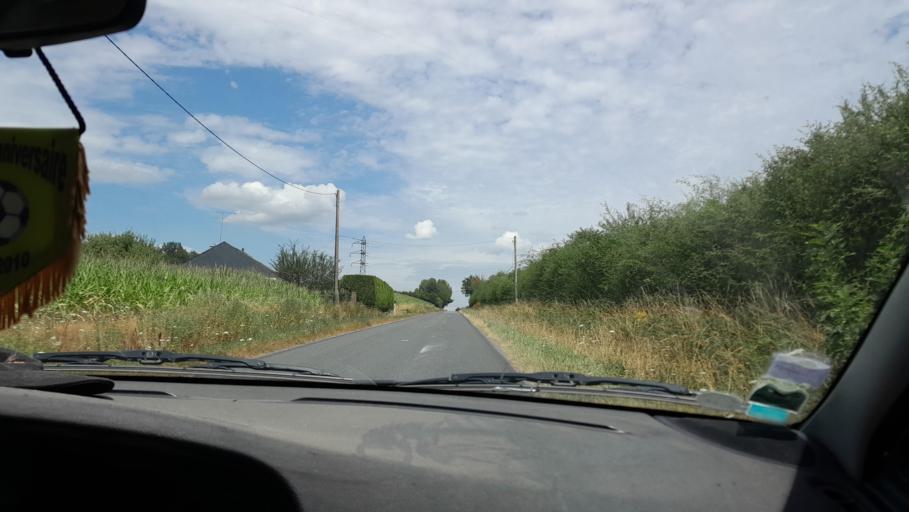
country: FR
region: Pays de la Loire
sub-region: Departement de la Mayenne
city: Saint-Pierre-la-Cour
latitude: 48.1241
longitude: -1.0245
